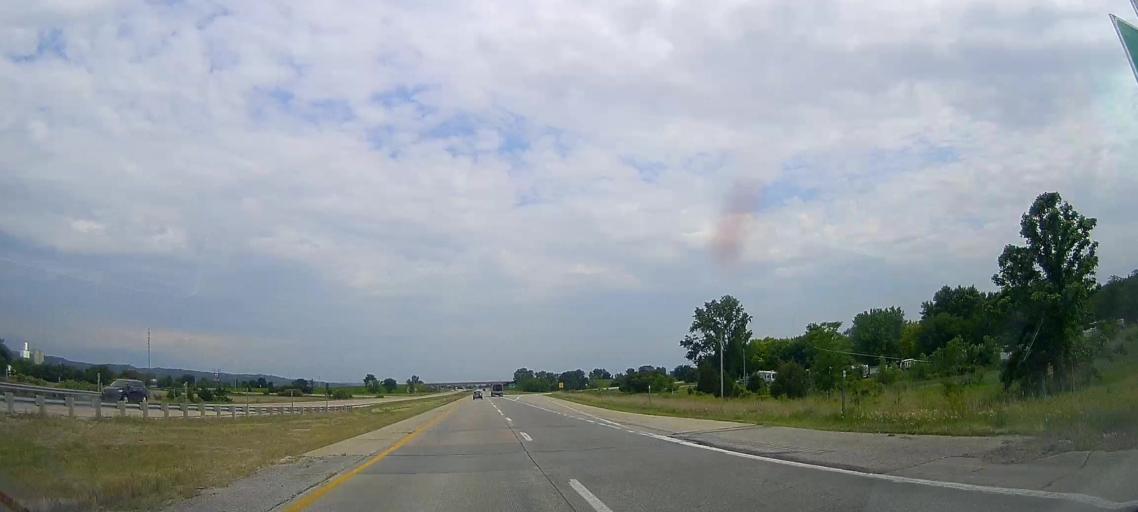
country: US
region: Nebraska
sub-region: Burt County
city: Tekamah
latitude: 41.8053
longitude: -96.0588
